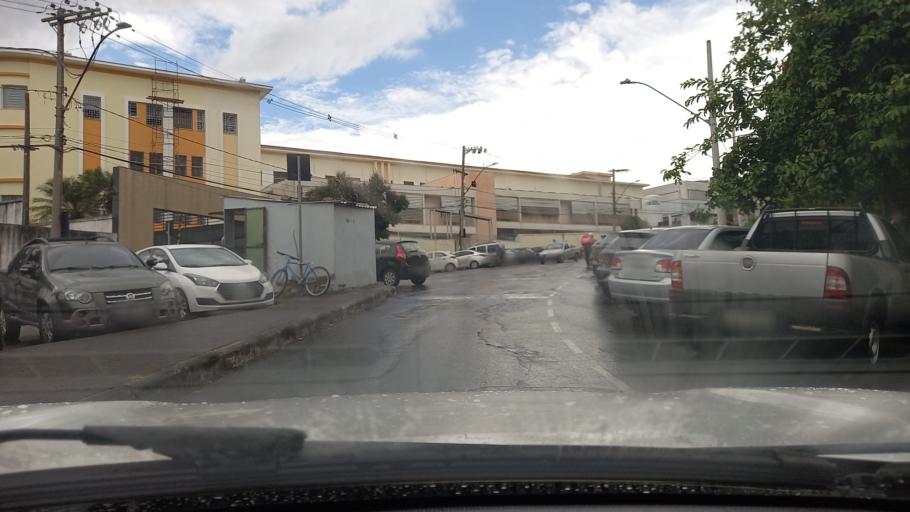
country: BR
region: Minas Gerais
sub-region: Belo Horizonte
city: Belo Horizonte
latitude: -19.9040
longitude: -43.9459
